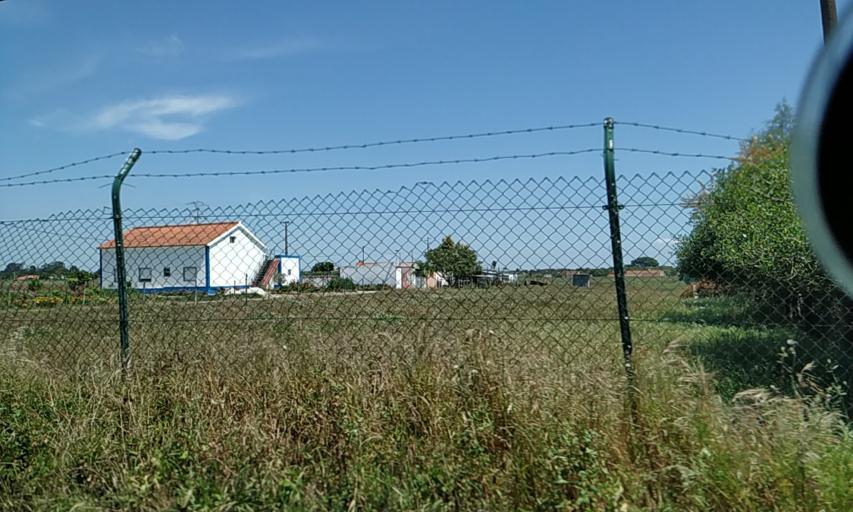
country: PT
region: Santarem
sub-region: Benavente
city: Poceirao
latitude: 38.6777
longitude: -8.7335
